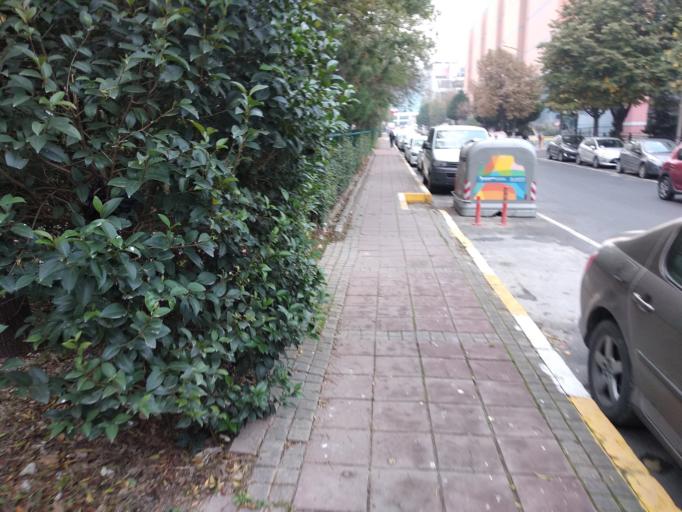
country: TR
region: Istanbul
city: Beylikduezue
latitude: 41.0108
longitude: 28.6500
